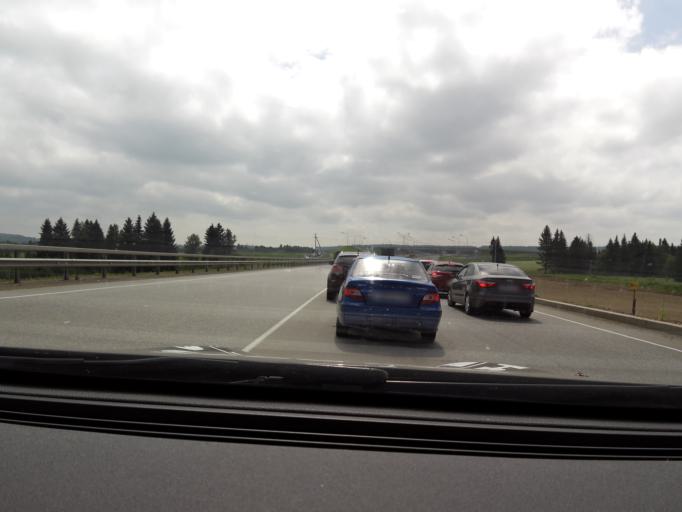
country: RU
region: Perm
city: Zvezdnyy
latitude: 57.7871
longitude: 56.3403
